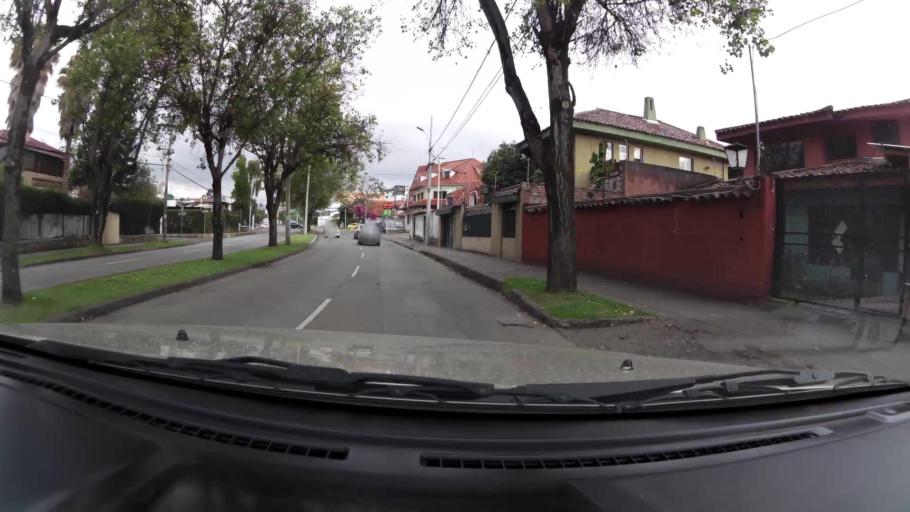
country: EC
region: Azuay
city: Cuenca
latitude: -2.9094
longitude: -79.0040
